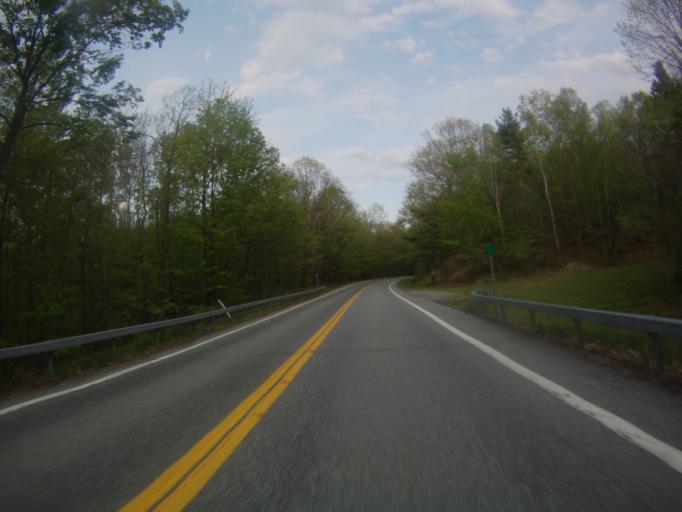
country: US
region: New York
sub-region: Essex County
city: Ticonderoga
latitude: 43.7602
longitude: -73.5375
